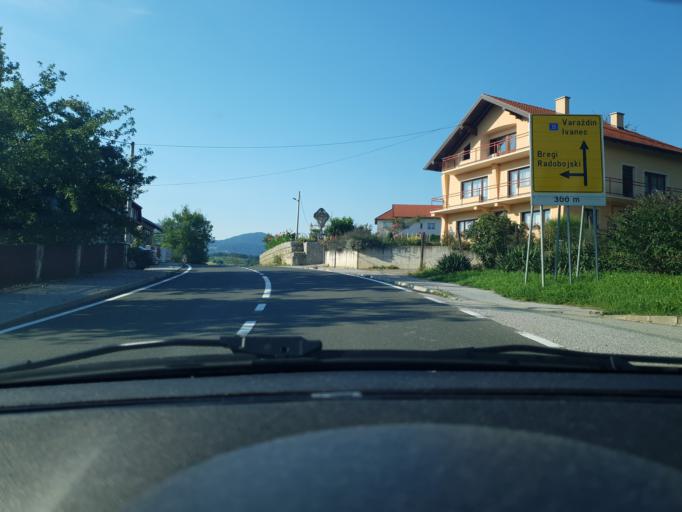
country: HR
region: Krapinsko-Zagorska
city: Mihovljan
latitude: 46.1284
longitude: 15.9380
